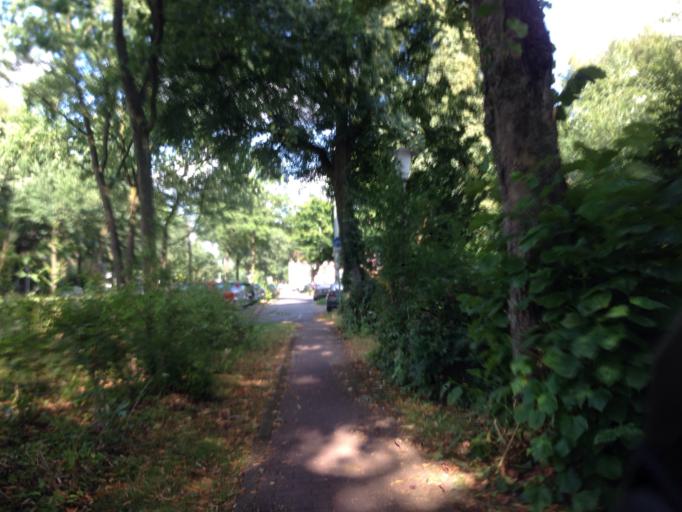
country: DE
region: Hamburg
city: Marienthal
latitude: 53.5832
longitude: 10.0728
